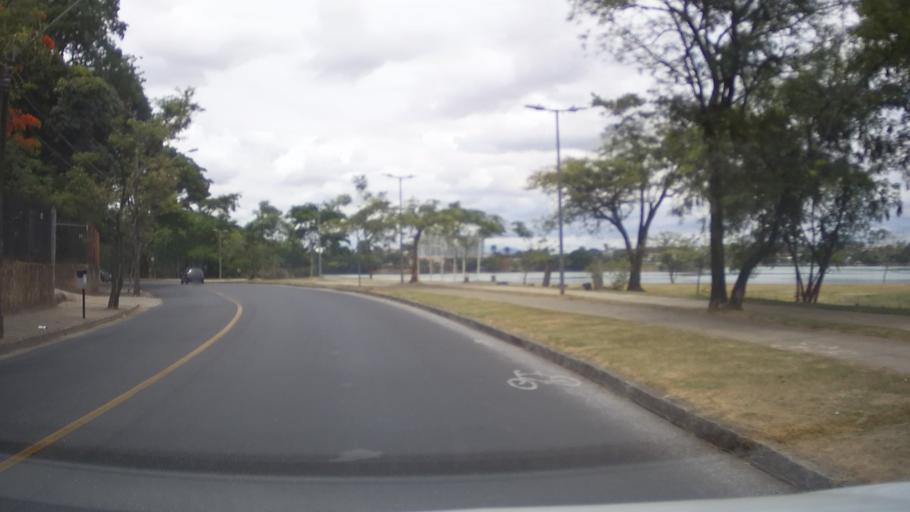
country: BR
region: Minas Gerais
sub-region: Belo Horizonte
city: Belo Horizonte
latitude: -19.8507
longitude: -43.9817
